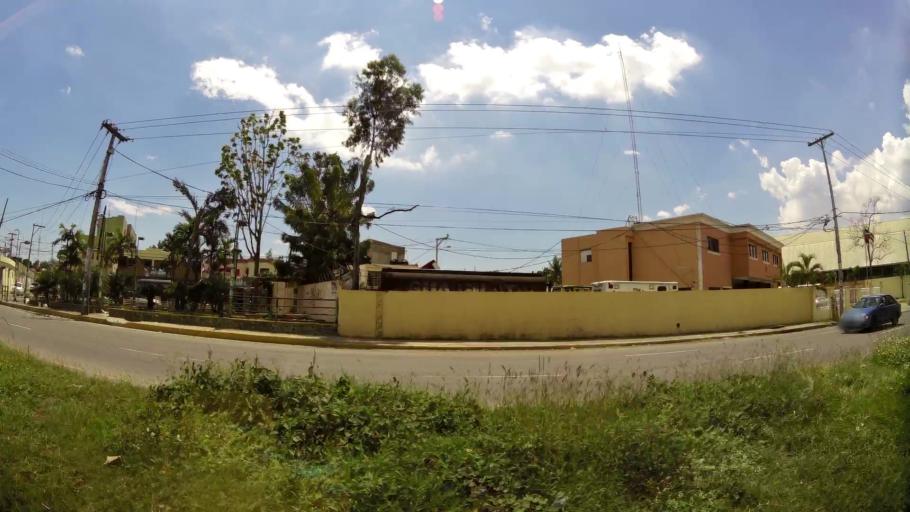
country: DO
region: Nacional
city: Ensanche Luperon
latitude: 18.5454
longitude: -69.8660
